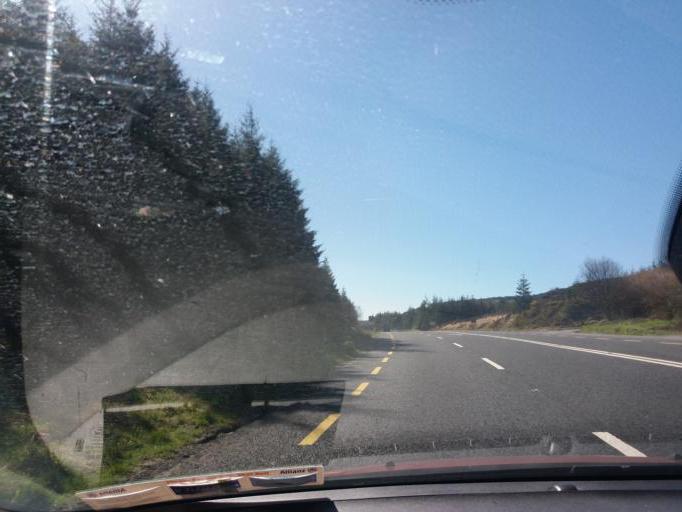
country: IE
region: Munster
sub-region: County Cork
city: Millstreet
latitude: 51.9716
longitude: -9.2525
